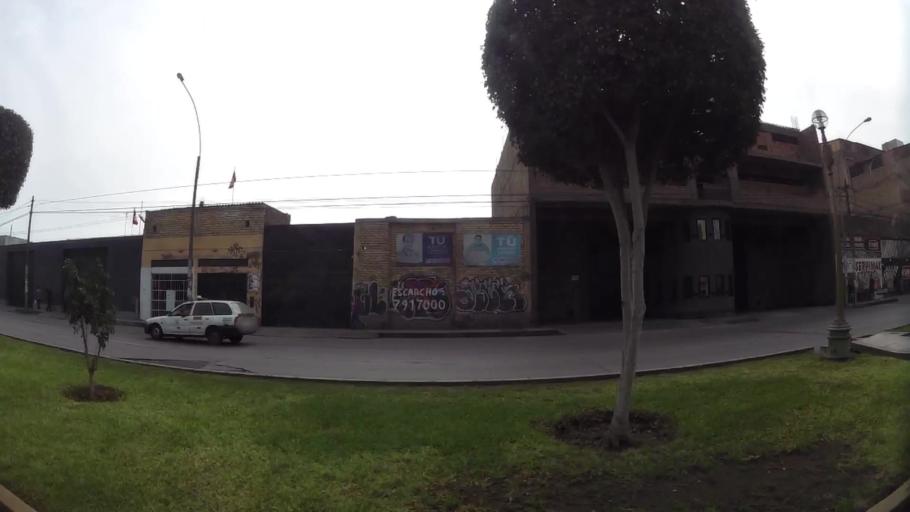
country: PE
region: Callao
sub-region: Callao
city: Callao
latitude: -12.0328
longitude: -77.0958
